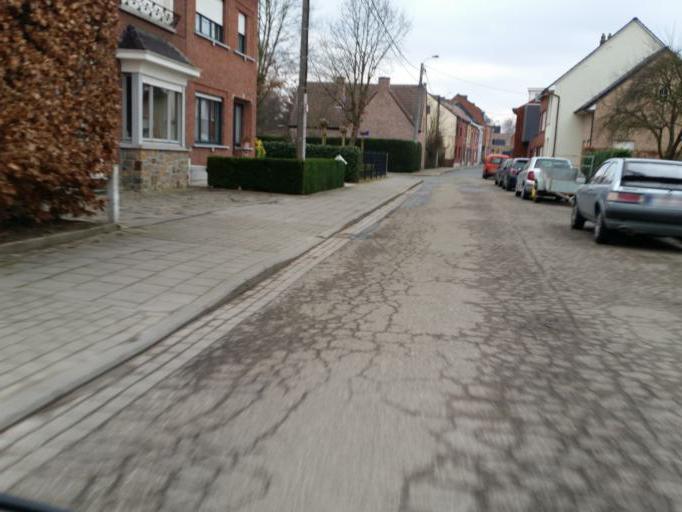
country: BE
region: Flanders
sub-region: Provincie Antwerpen
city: Bonheiden
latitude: 51.0056
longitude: 4.5124
